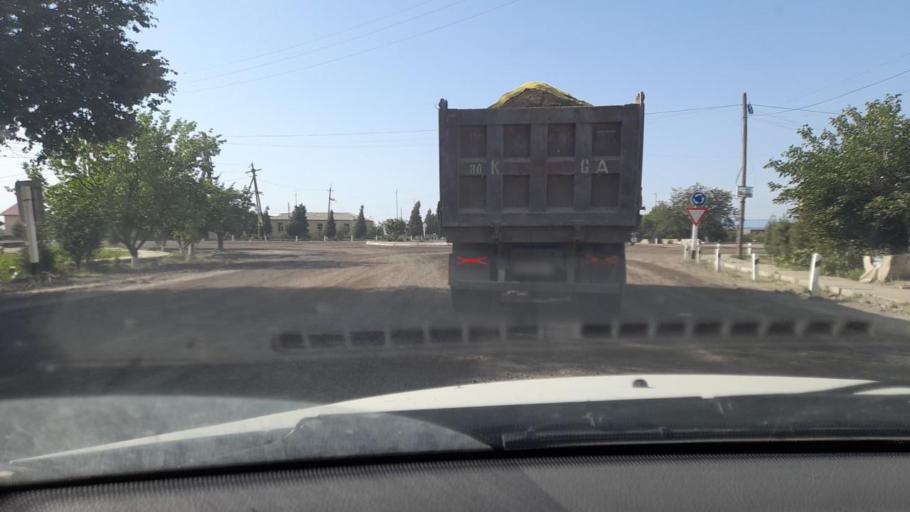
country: UZ
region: Bukhara
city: Romiton
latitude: 40.0465
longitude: 64.3288
